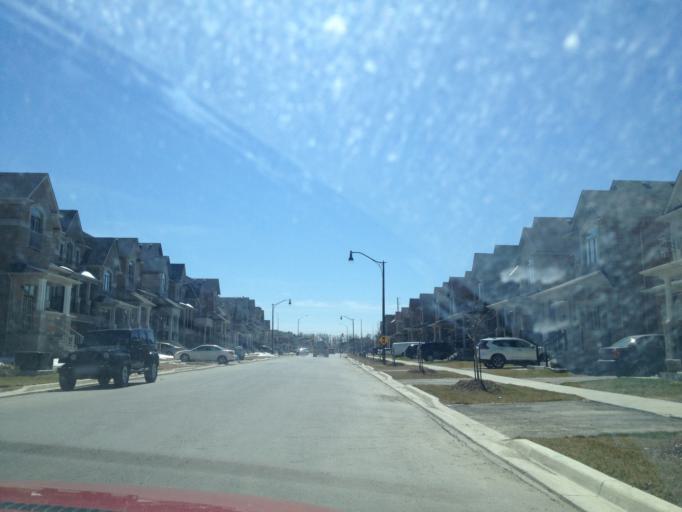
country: CA
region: Ontario
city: Brampton
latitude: 43.7033
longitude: -79.8513
